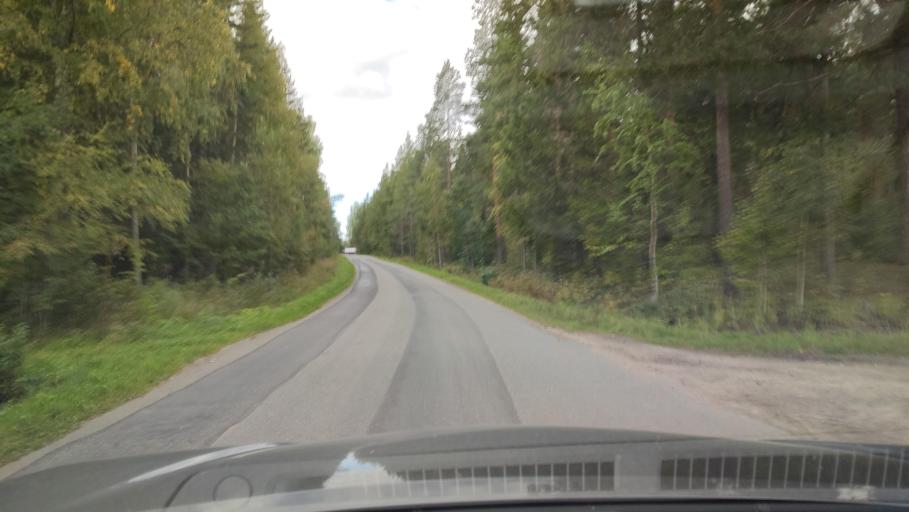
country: FI
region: Southern Ostrobothnia
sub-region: Suupohja
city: Karijoki
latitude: 62.2366
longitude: 21.5992
